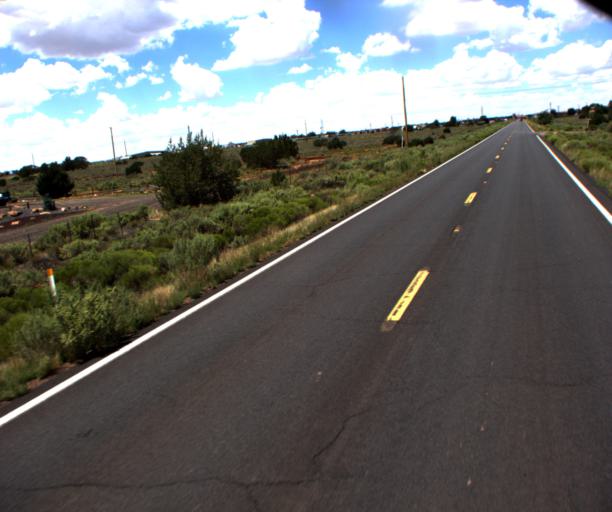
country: US
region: Arizona
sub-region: Coconino County
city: Williams
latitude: 35.6448
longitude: -112.1310
